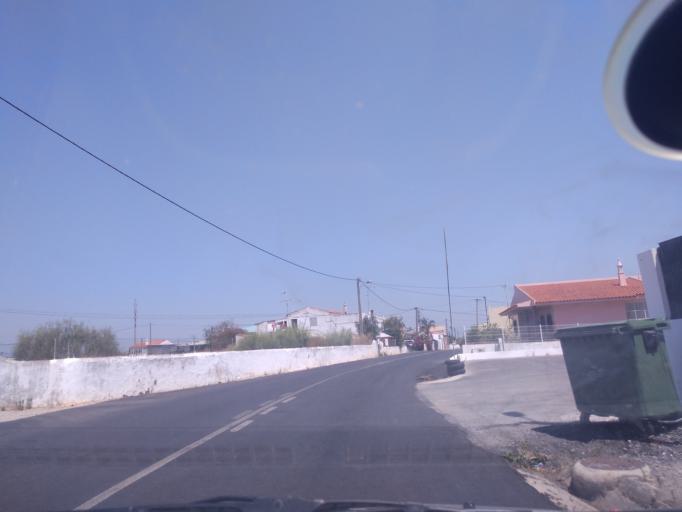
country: PT
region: Faro
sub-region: Faro
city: Faro
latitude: 37.0522
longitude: -7.9435
